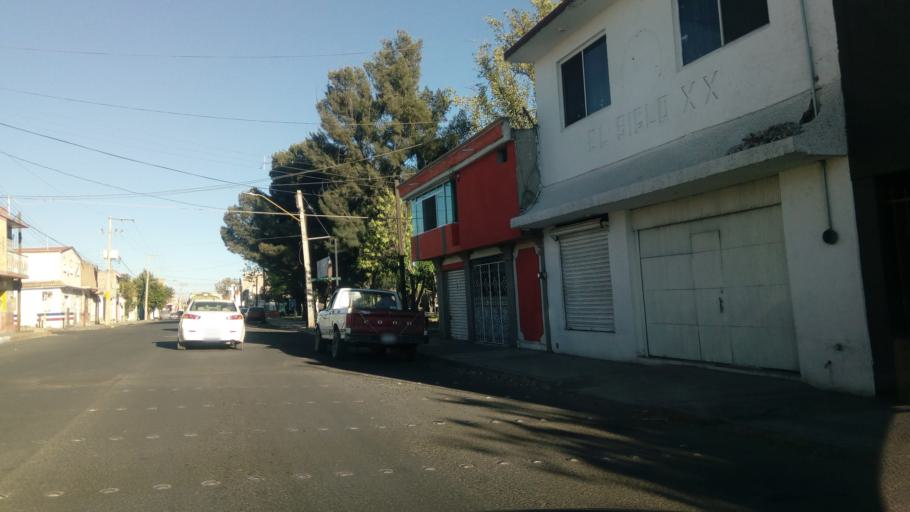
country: MX
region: Durango
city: Victoria de Durango
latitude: 24.0120
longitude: -104.6768
